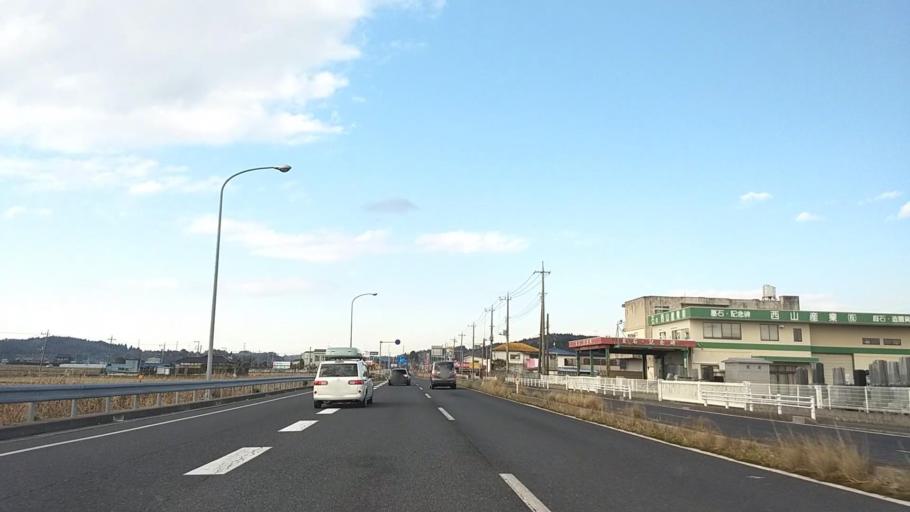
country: JP
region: Chiba
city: Togane
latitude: 35.5537
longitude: 140.3473
